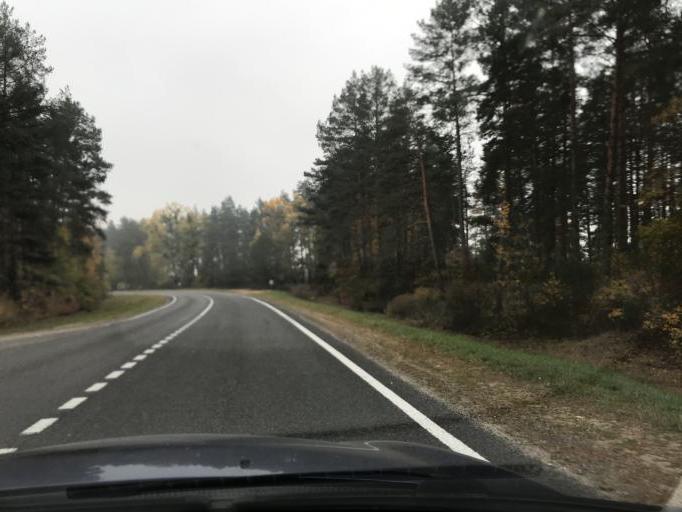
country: BY
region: Grodnenskaya
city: Hrodna
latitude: 53.8487
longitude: 23.8905
